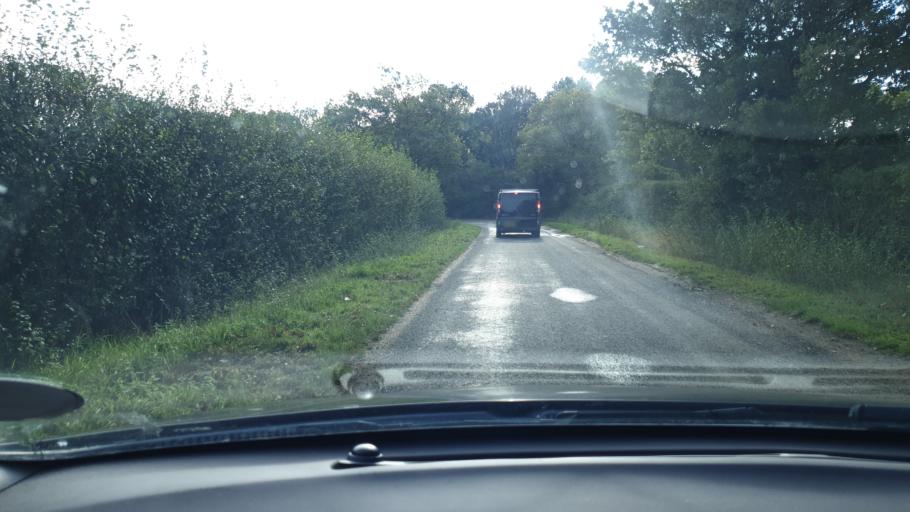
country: GB
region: England
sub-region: Essex
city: Alresford
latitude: 51.8611
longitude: 1.0201
